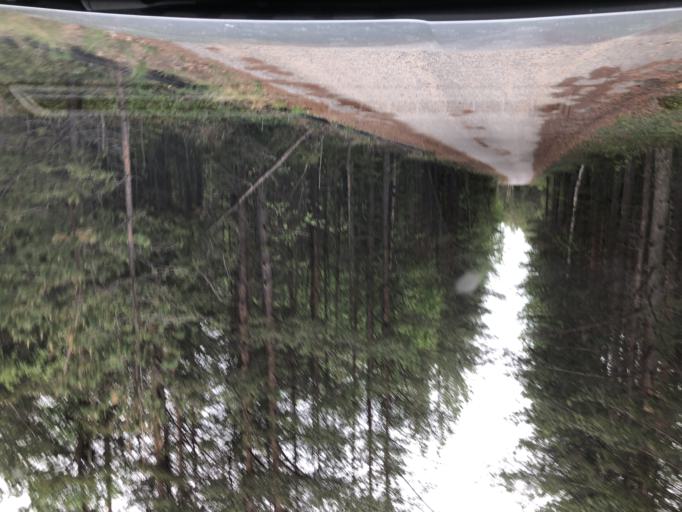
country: SE
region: Norrbotten
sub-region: Pitea Kommun
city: Pitea
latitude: 65.2351
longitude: 21.5141
